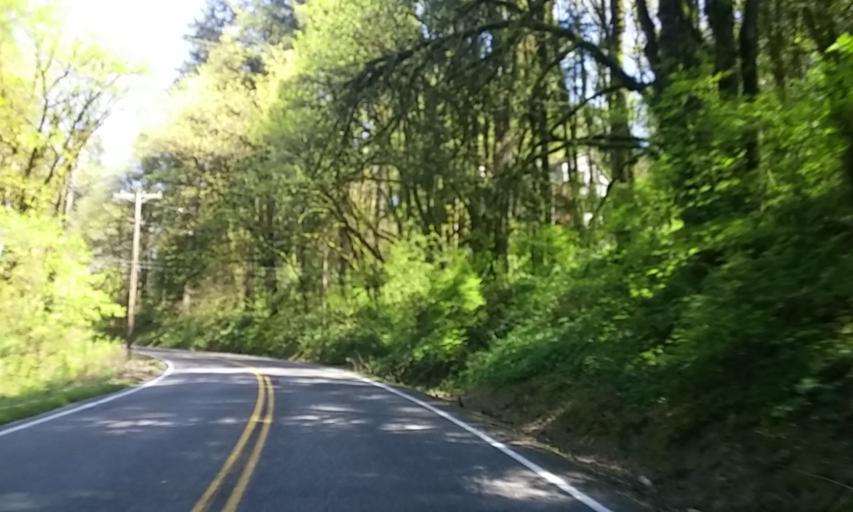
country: US
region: Oregon
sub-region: Washington County
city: West Haven
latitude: 45.5304
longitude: -122.7575
